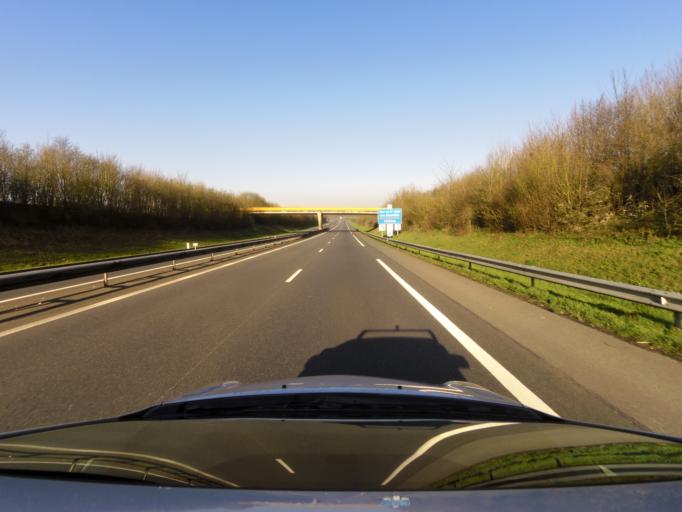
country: FR
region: Lower Normandy
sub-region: Departement du Calvados
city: Cahagnes
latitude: 49.0480
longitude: -0.7639
